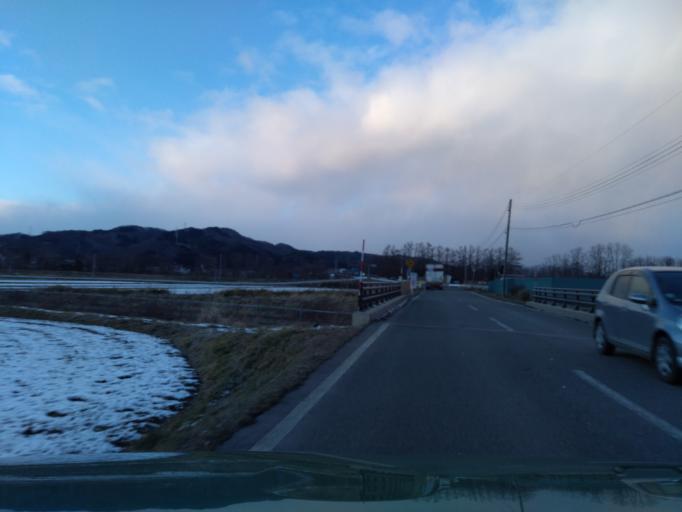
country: JP
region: Iwate
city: Shizukuishi
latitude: 39.6936
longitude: 141.0650
